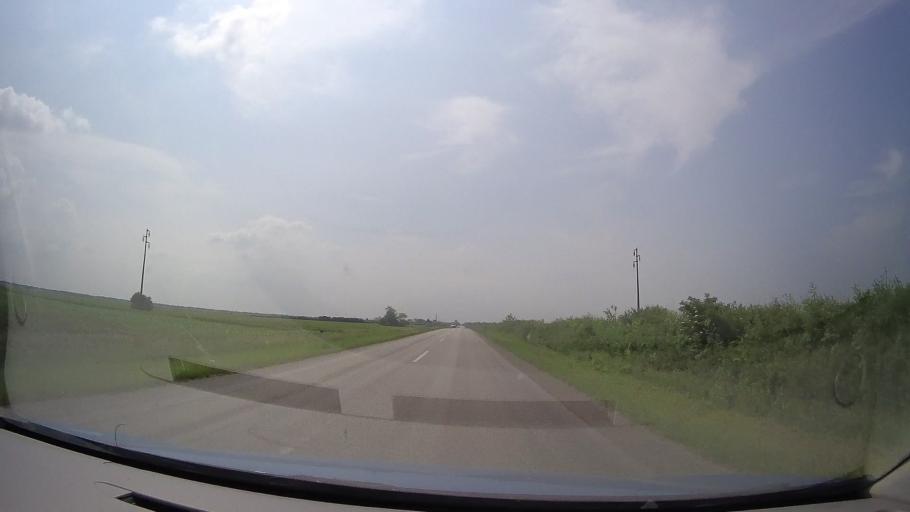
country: RS
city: Crepaja
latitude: 44.9612
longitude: 20.6567
